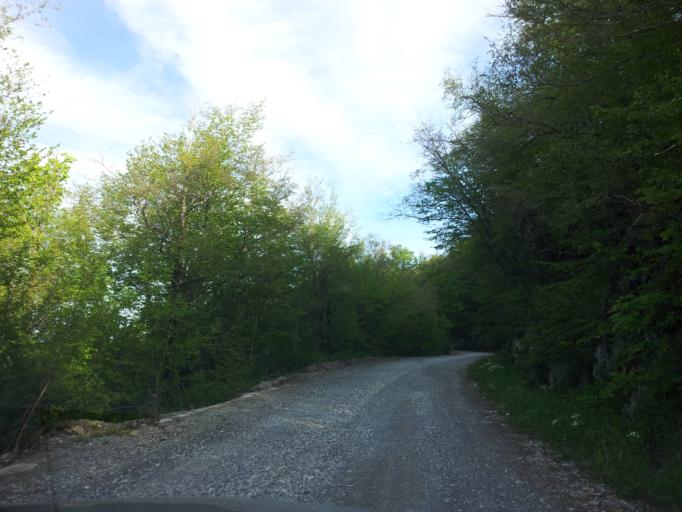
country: HR
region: Zadarska
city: Obrovac
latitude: 44.3021
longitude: 15.6622
